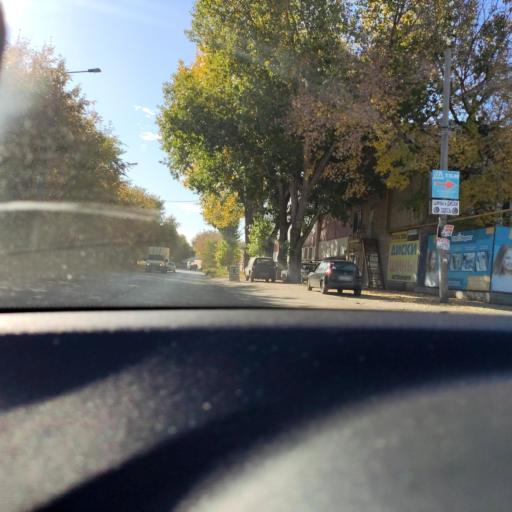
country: RU
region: Samara
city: Petra-Dubrava
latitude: 53.2389
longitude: 50.2959
